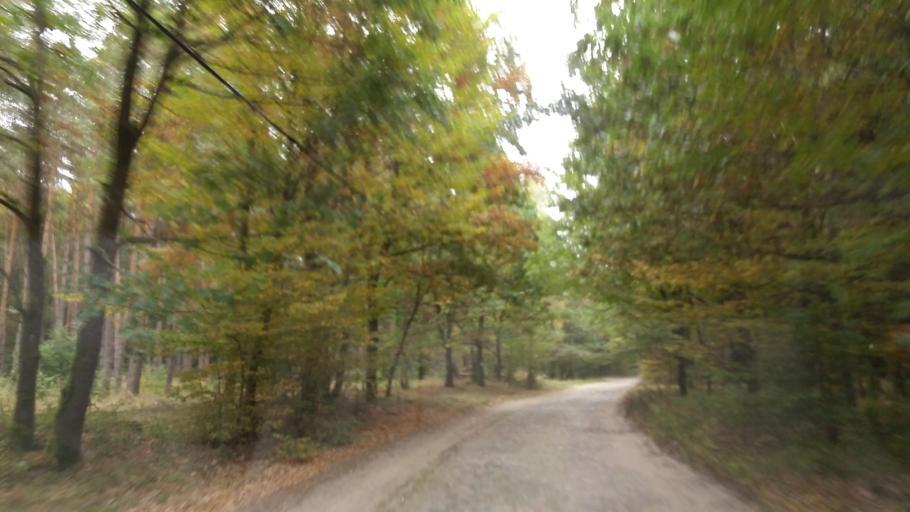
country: PL
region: West Pomeranian Voivodeship
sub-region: Powiat mysliborski
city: Barlinek
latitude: 52.9385
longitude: 15.2558
